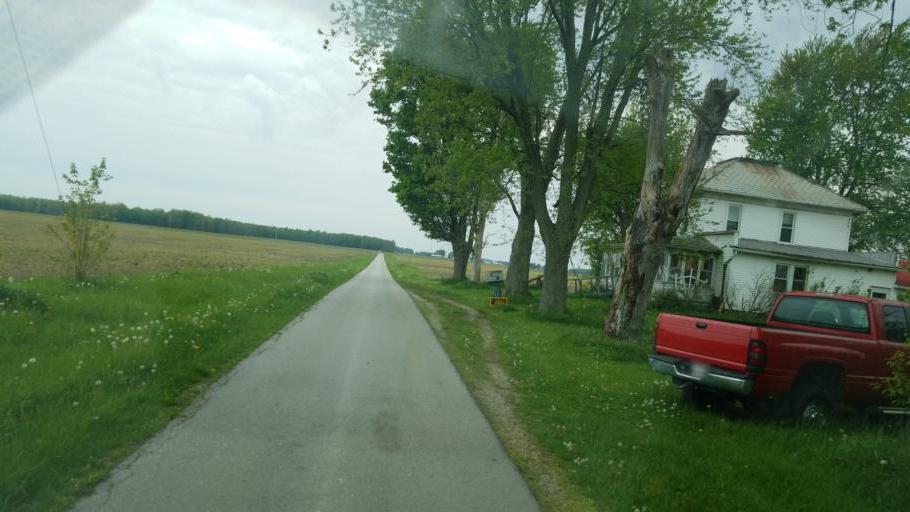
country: US
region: Ohio
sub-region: Huron County
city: Willard
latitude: 41.0190
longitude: -82.8549
